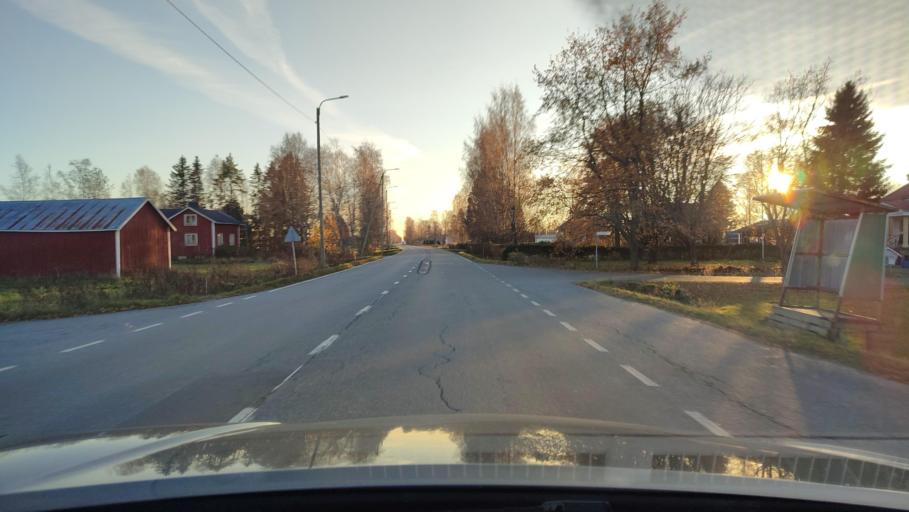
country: FI
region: Ostrobothnia
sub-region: Sydosterbotten
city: Naerpes
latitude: 62.6045
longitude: 21.4588
